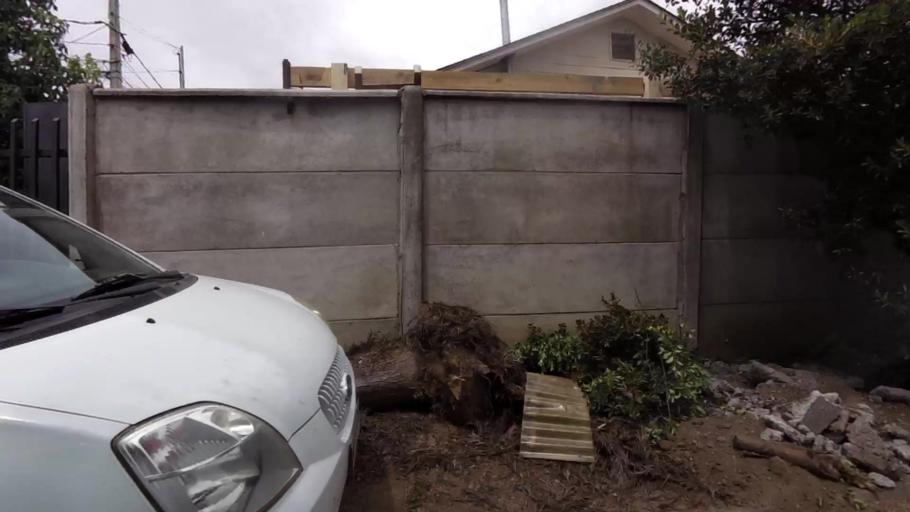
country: CL
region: O'Higgins
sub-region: Provincia de Cachapoal
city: Graneros
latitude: -34.0713
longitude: -70.7197
